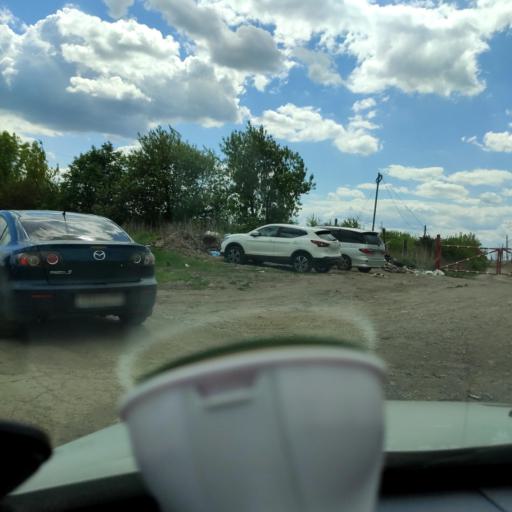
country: RU
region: Samara
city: Petra-Dubrava
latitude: 53.2661
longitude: 50.3150
